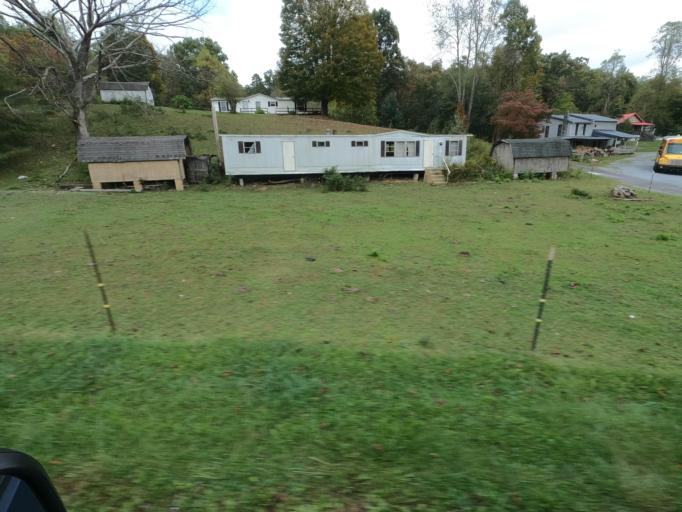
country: US
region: Tennessee
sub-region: Carter County
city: Elizabethton
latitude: 36.2631
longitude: -82.2024
